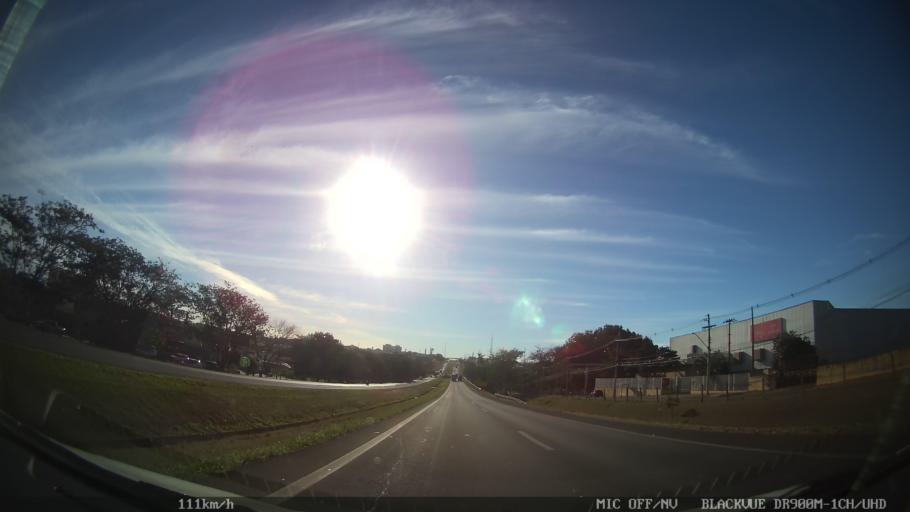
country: BR
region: Sao Paulo
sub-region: Sao Jose Do Rio Preto
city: Sao Jose do Rio Preto
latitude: -20.8434
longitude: -49.3503
